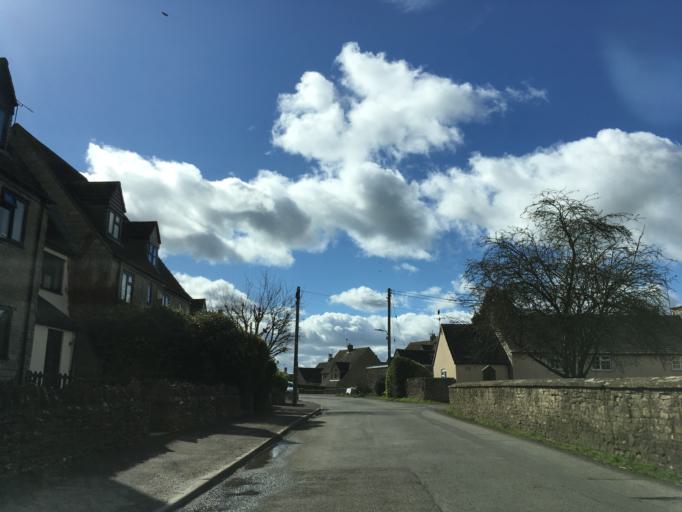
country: GB
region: England
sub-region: Gloucestershire
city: Wotton-under-Edge
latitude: 51.6048
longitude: -2.3348
